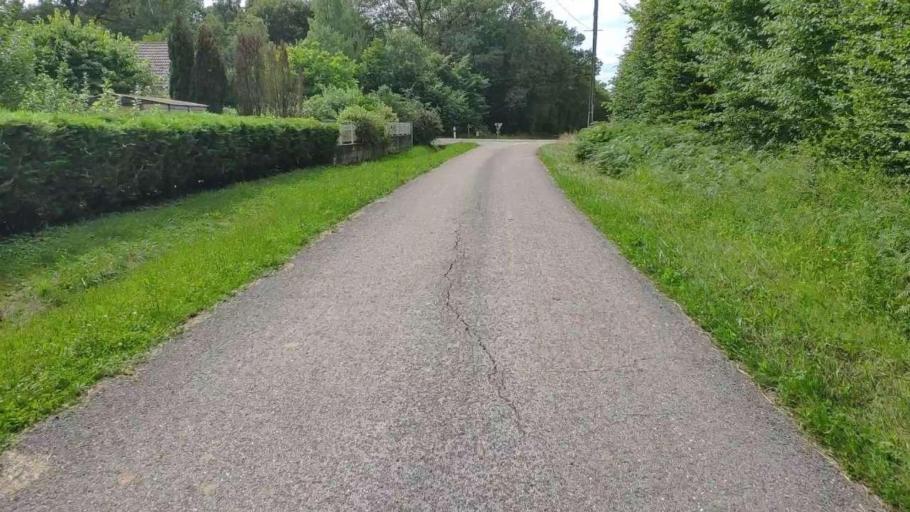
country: FR
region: Franche-Comte
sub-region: Departement du Jura
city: Bletterans
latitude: 46.7956
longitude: 5.4496
